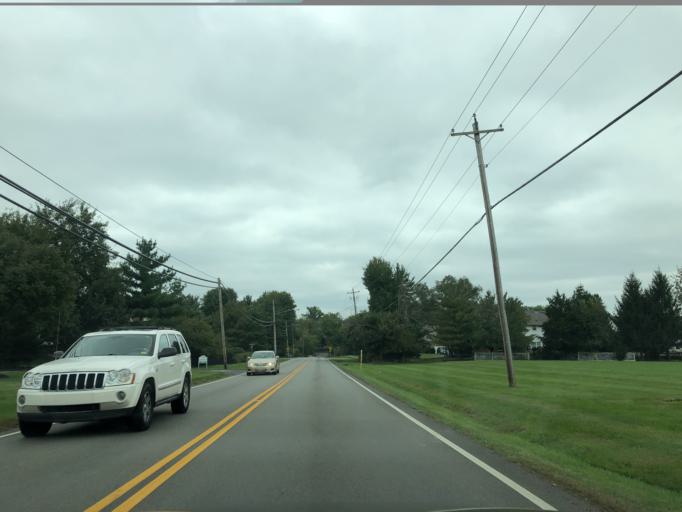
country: US
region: Ohio
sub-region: Warren County
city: Loveland Park
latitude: 39.2873
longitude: -84.2830
